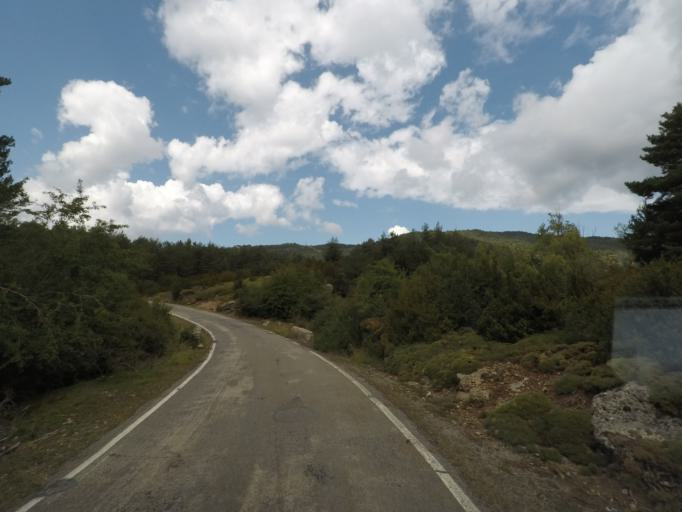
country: ES
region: Aragon
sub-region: Provincia de Huesca
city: Fiscal
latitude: 42.4009
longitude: -0.0515
